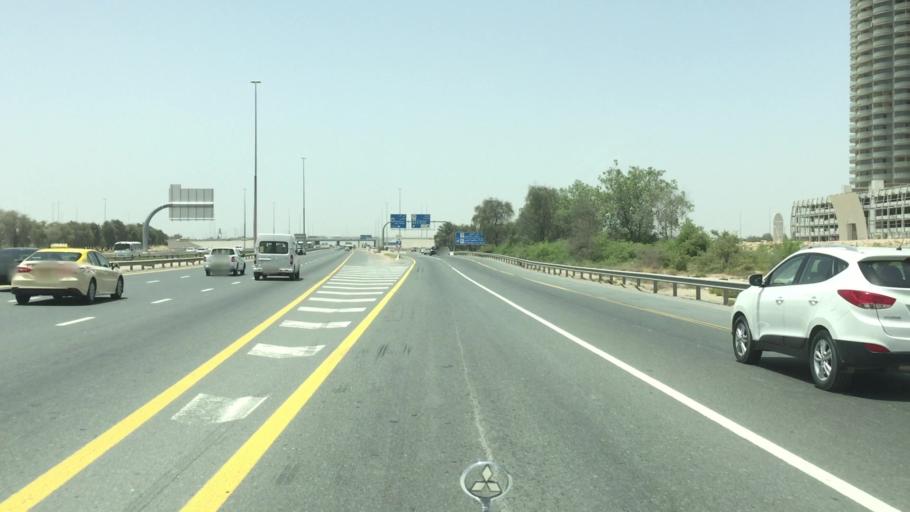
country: AE
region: Dubai
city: Dubai
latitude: 25.1145
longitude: 55.3698
